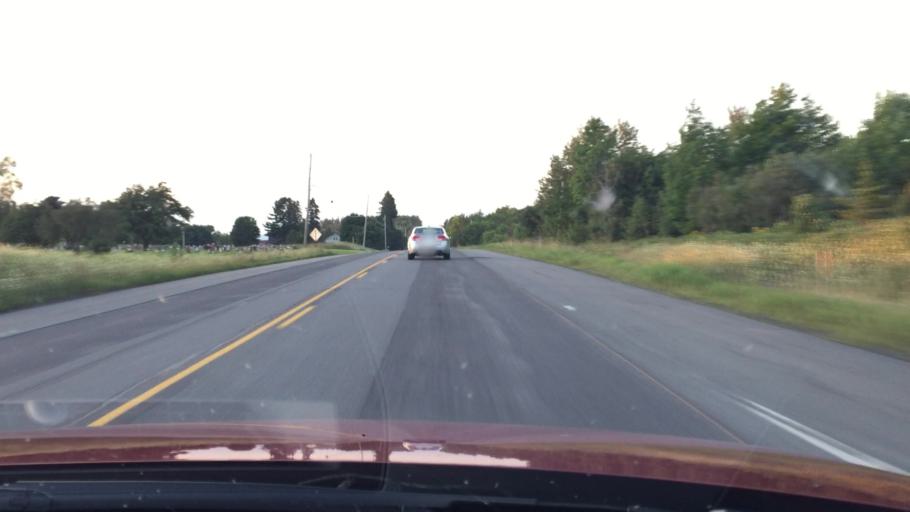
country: US
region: Maine
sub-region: Aroostook County
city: Houlton
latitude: 46.3411
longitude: -67.8419
